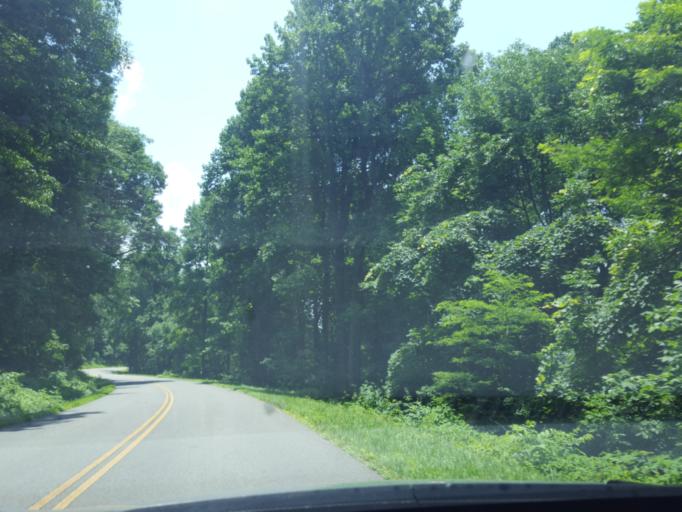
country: US
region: Virginia
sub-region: Nelson County
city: Nellysford
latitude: 37.9212
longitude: -78.9674
